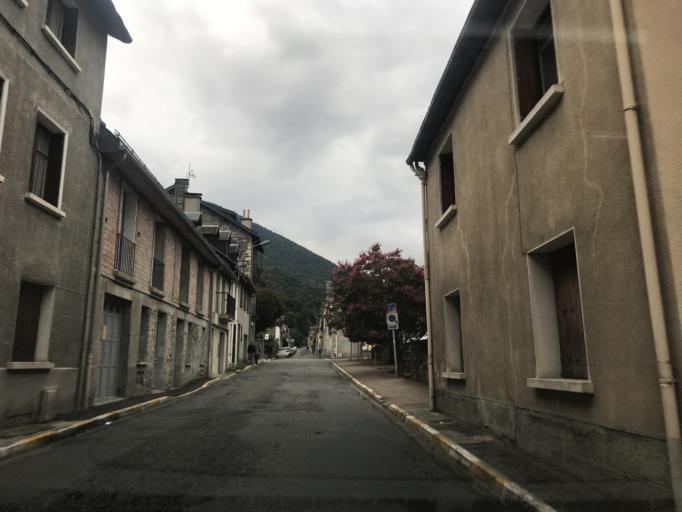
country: FR
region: Midi-Pyrenees
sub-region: Departement de la Haute-Garonne
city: Bagneres-de-Luchon
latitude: 42.7918
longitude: 0.5882
